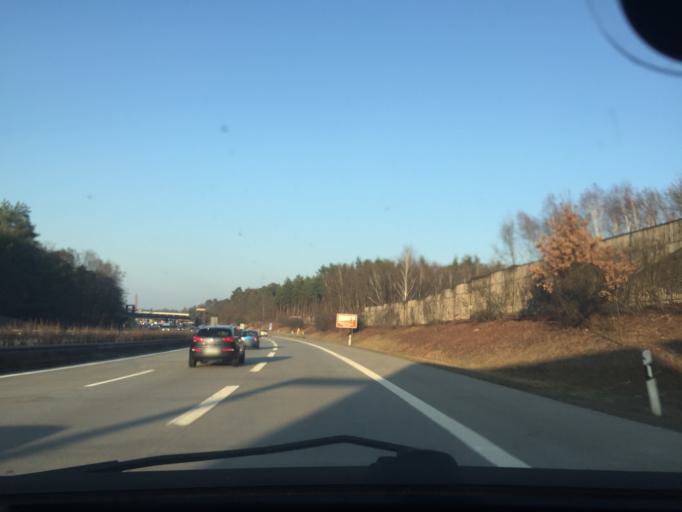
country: DE
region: Berlin
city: Nikolassee
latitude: 52.4120
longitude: 13.1974
